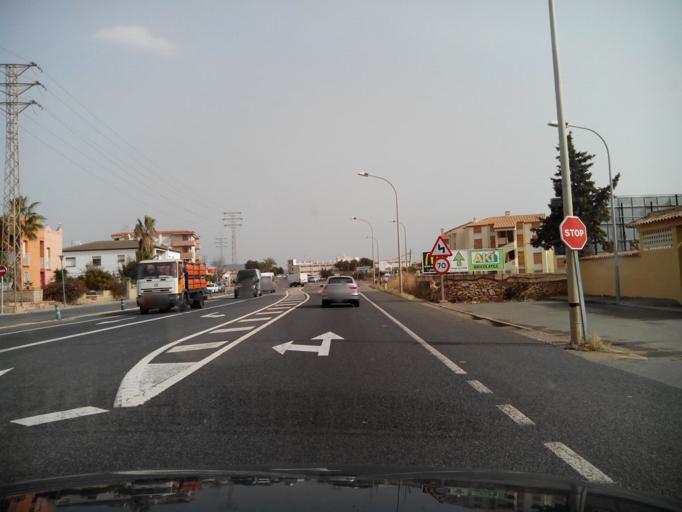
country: ES
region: Catalonia
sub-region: Provincia de Tarragona
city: Creixell
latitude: 41.1581
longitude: 1.4331
